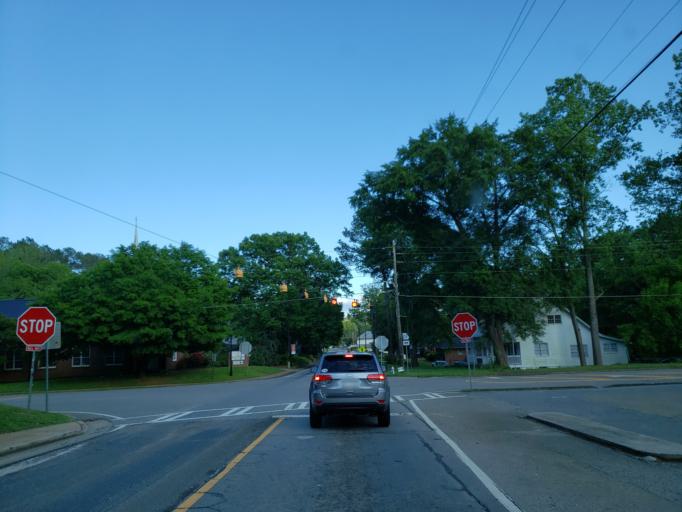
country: US
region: Georgia
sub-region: Cherokee County
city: Canton
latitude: 34.3169
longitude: -84.5531
